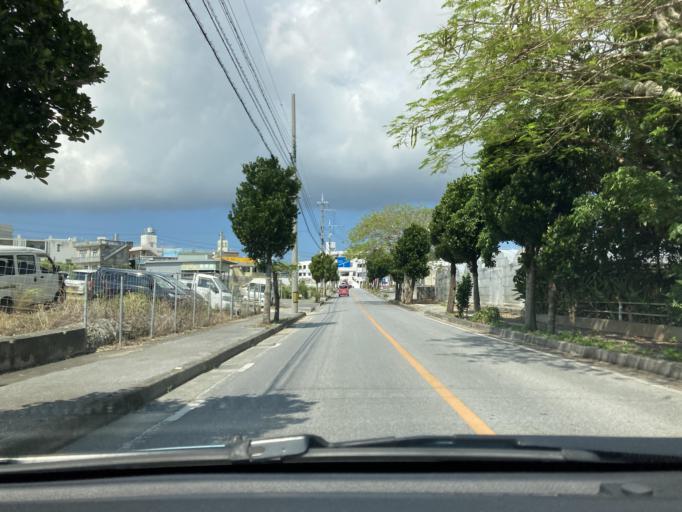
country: JP
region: Okinawa
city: Tomigusuku
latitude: 26.1751
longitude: 127.7206
